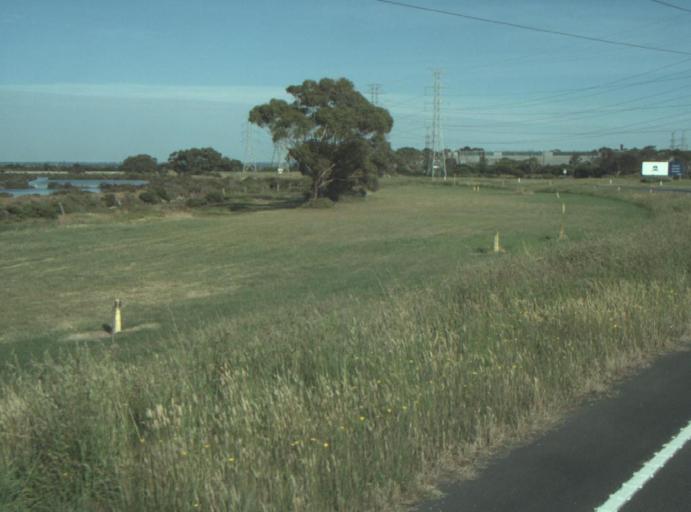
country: AU
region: Victoria
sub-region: Greater Geelong
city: East Geelong
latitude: -38.1420
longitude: 144.4277
